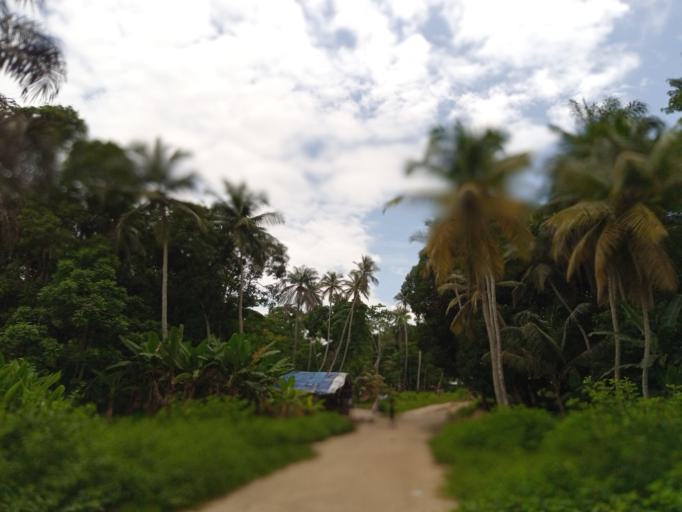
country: SL
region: Northern Province
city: Masoyila
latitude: 8.5595
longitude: -13.1701
